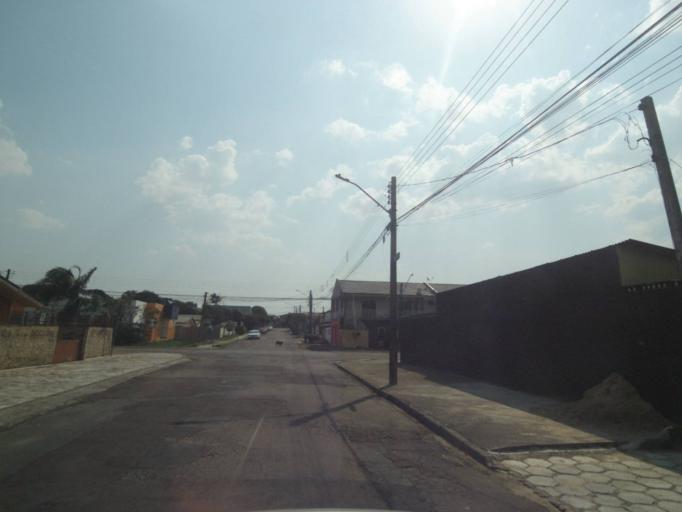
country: BR
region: Parana
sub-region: Sao Jose Dos Pinhais
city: Sao Jose dos Pinhais
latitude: -25.5407
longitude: -49.2401
